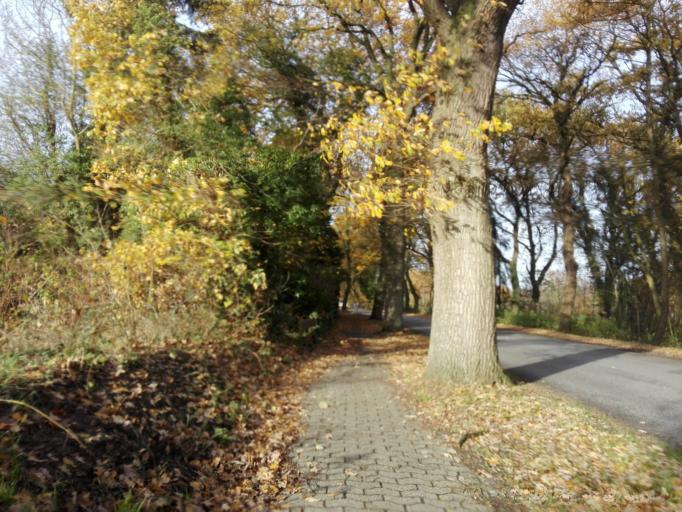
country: DE
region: Lower Saxony
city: Wiefelstede
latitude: 53.2839
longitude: 8.1382
